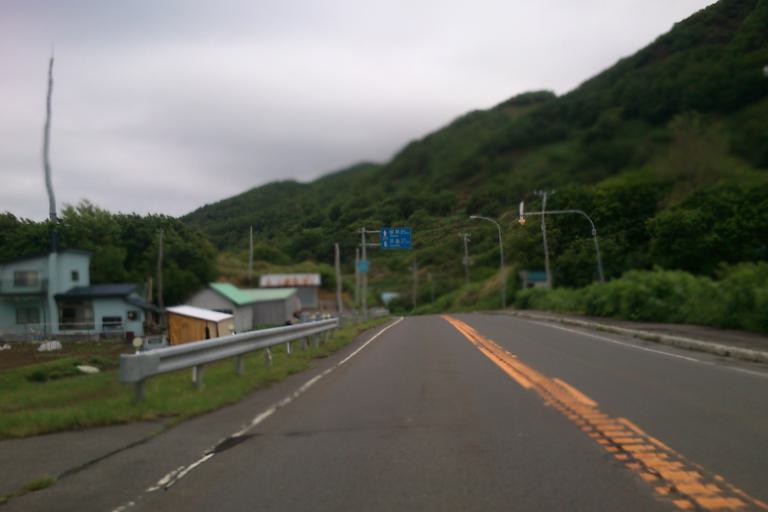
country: JP
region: Hokkaido
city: Ishikari
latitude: 43.4186
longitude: 141.4295
